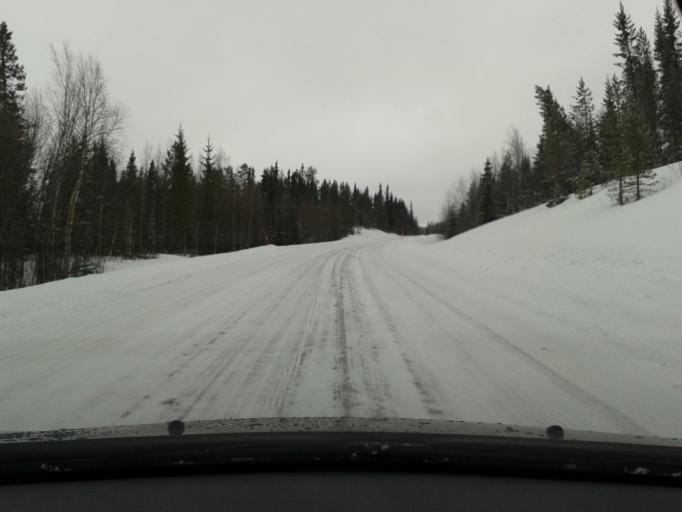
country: SE
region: Vaesterbotten
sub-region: Vilhelmina Kommun
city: Sjoberg
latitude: 64.8218
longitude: 15.9635
